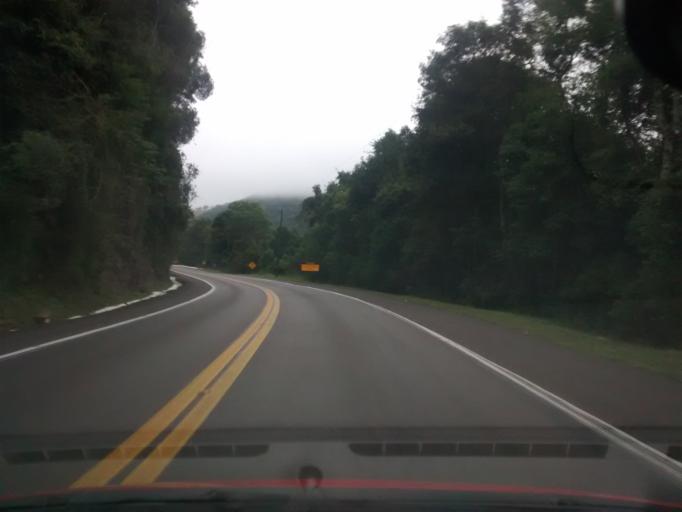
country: BR
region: Rio Grande do Sul
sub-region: Vacaria
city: Estrela
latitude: -28.2204
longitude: -50.7580
